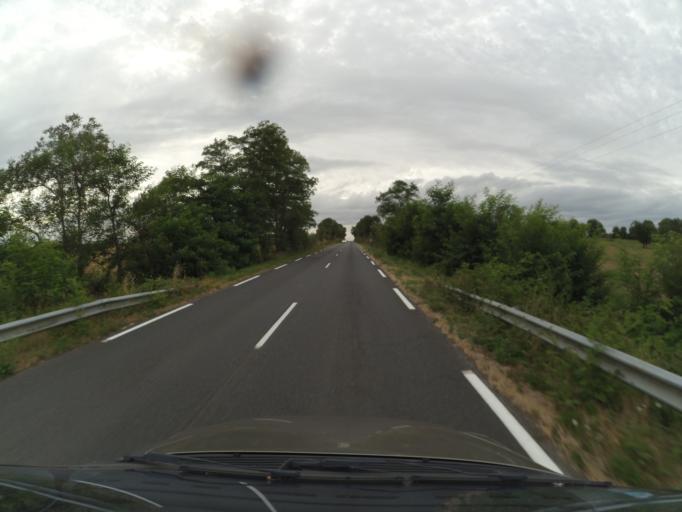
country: FR
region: Pays de la Loire
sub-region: Departement de Maine-et-Loire
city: Le Longeron
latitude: 47.0268
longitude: -1.0702
